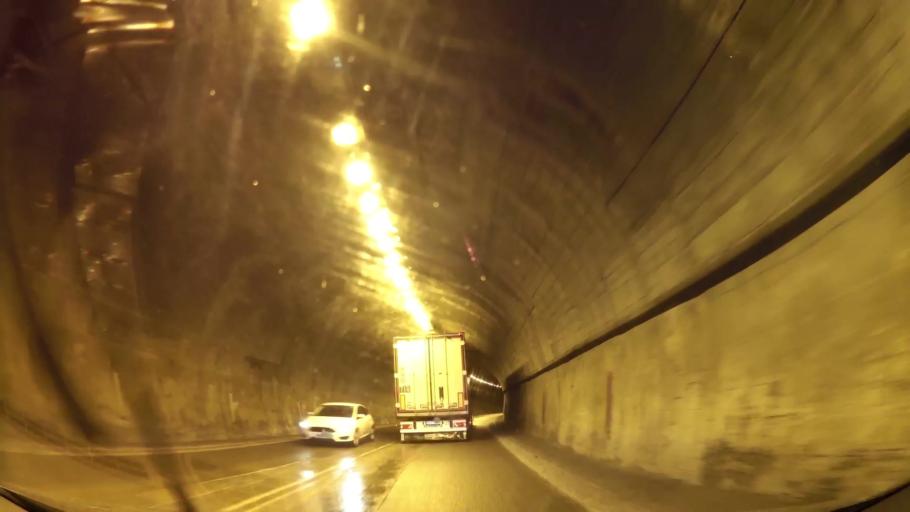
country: RS
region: Central Serbia
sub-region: Pcinjski Okrug
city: Vladicin Han
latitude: 42.7496
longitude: 22.0653
